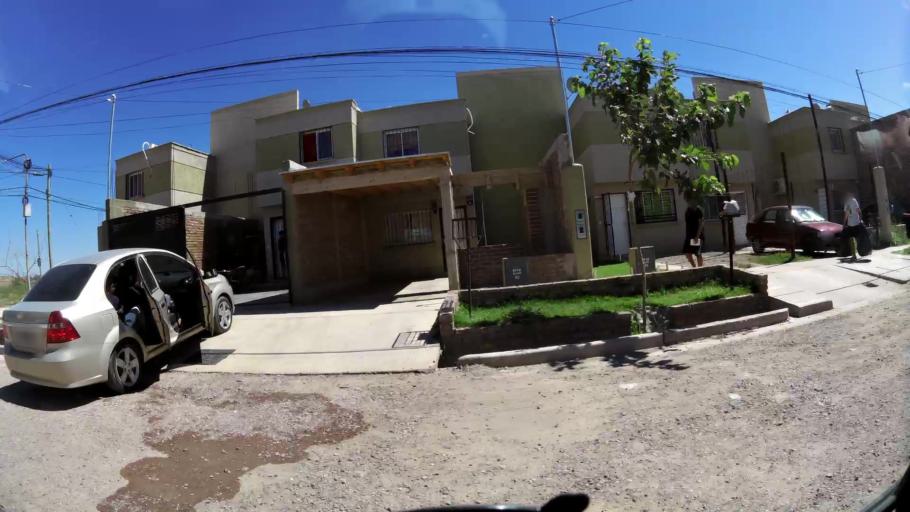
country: AR
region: Mendoza
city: Las Heras
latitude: -32.8457
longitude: -68.8517
